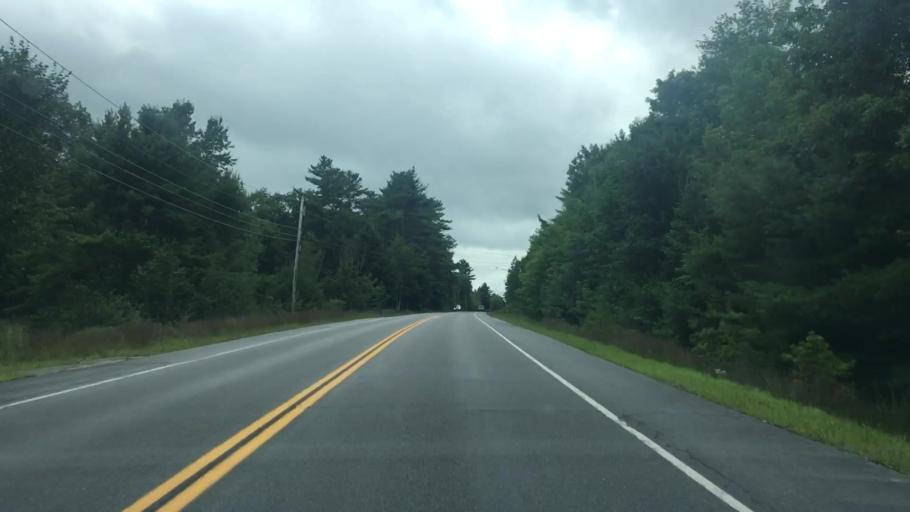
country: US
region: Maine
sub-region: York County
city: Cornish
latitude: 43.7479
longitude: -70.8128
